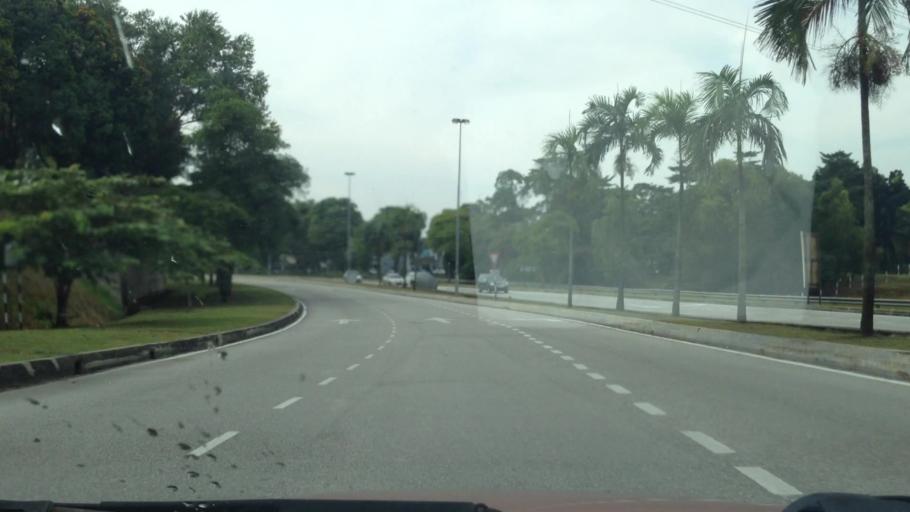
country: MY
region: Selangor
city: Subang Jaya
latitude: 3.0460
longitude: 101.5698
